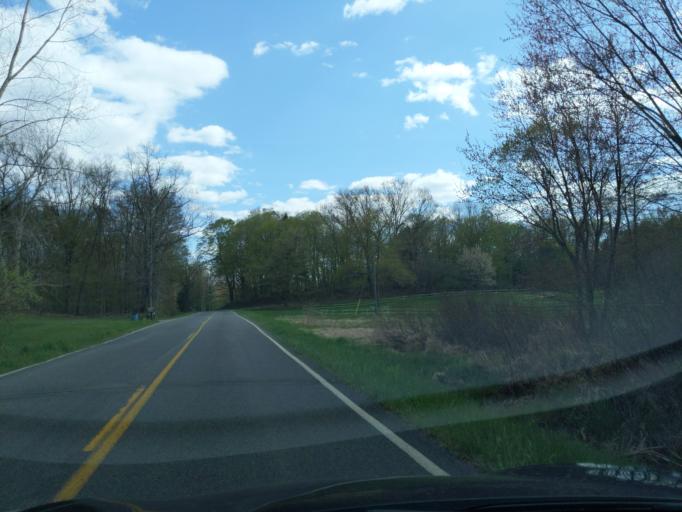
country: US
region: Michigan
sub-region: Ingham County
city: Leslie
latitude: 42.3994
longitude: -84.5417
